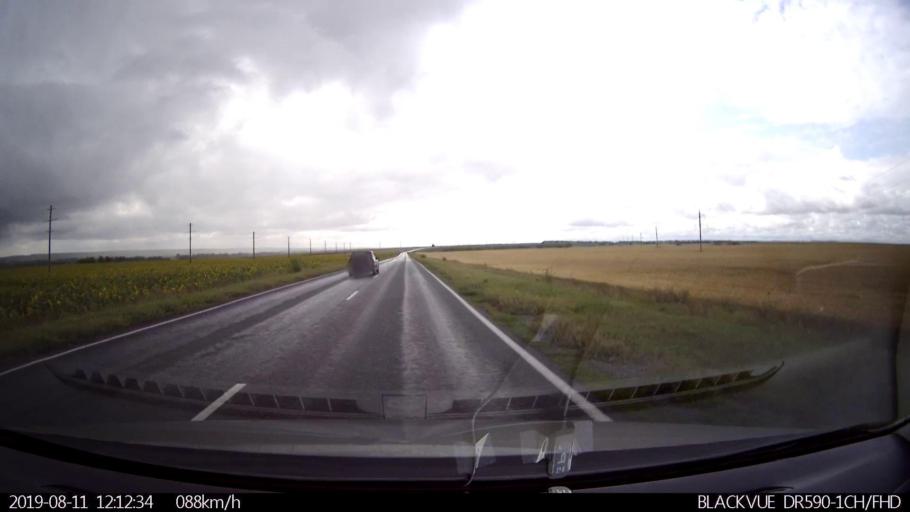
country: RU
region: Ulyanovsk
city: Silikatnyy
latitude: 53.9715
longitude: 47.9961
